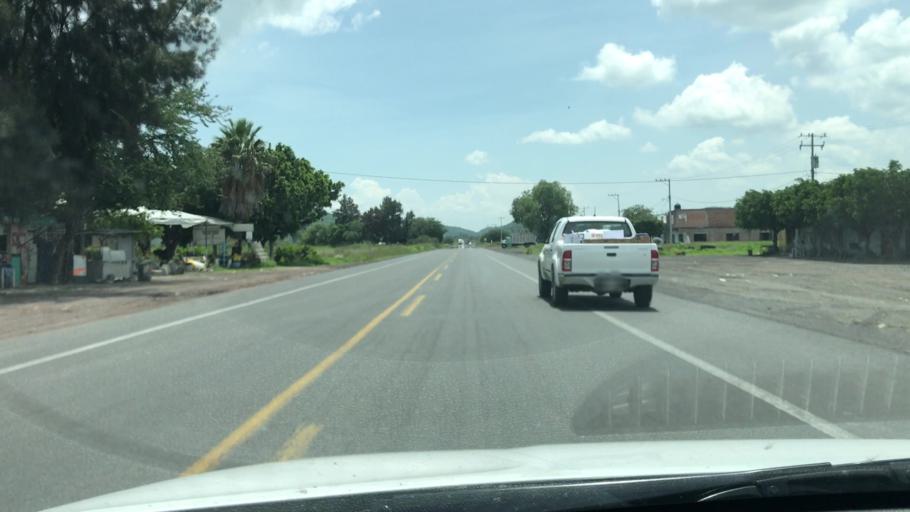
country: MX
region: Michoacan
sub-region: Yurecuaro
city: Yurecuaro
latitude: 20.3246
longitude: -102.2774
